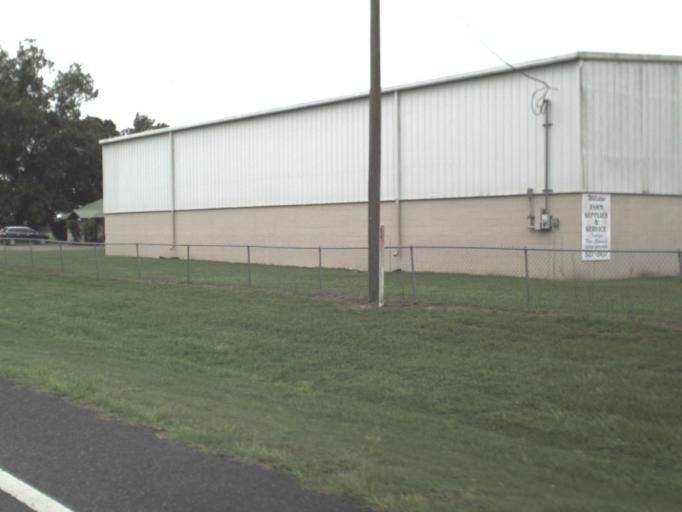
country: US
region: Florida
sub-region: Levy County
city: Williston
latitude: 29.3572
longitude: -82.4558
